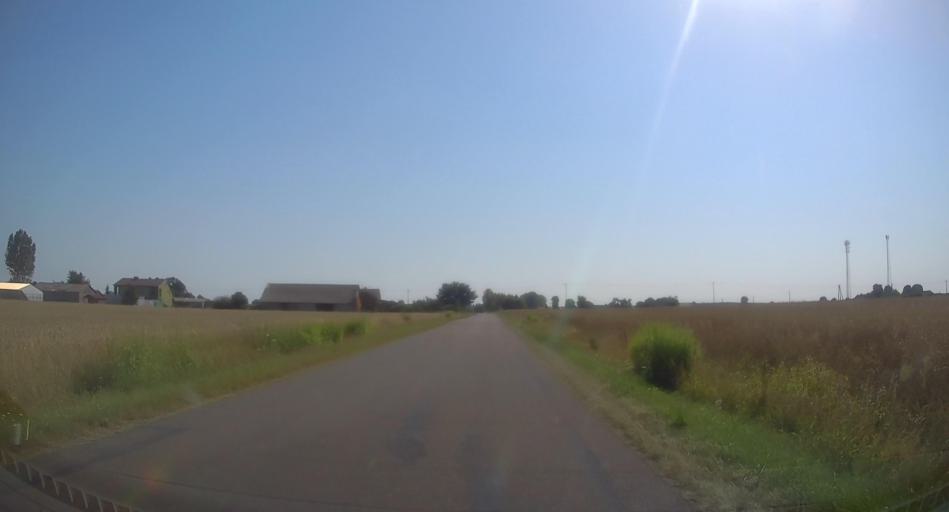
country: PL
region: Lodz Voivodeship
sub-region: Powiat skierniewicki
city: Kaweczyn Nowy
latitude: 51.8807
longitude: 20.2178
